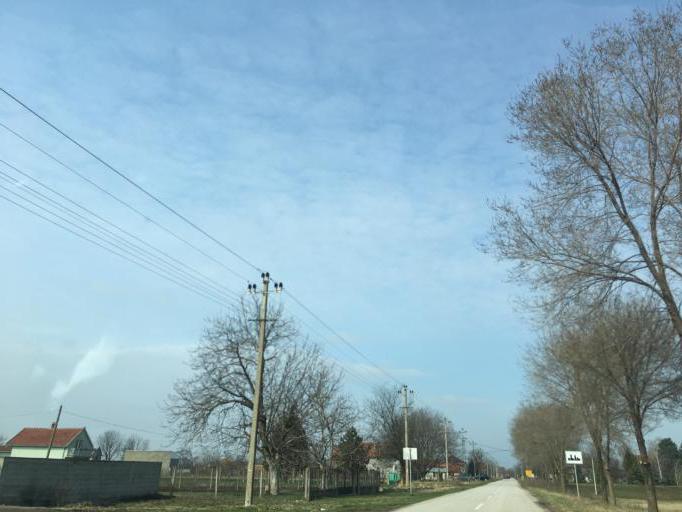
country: RS
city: Centa
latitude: 45.0992
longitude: 20.4021
